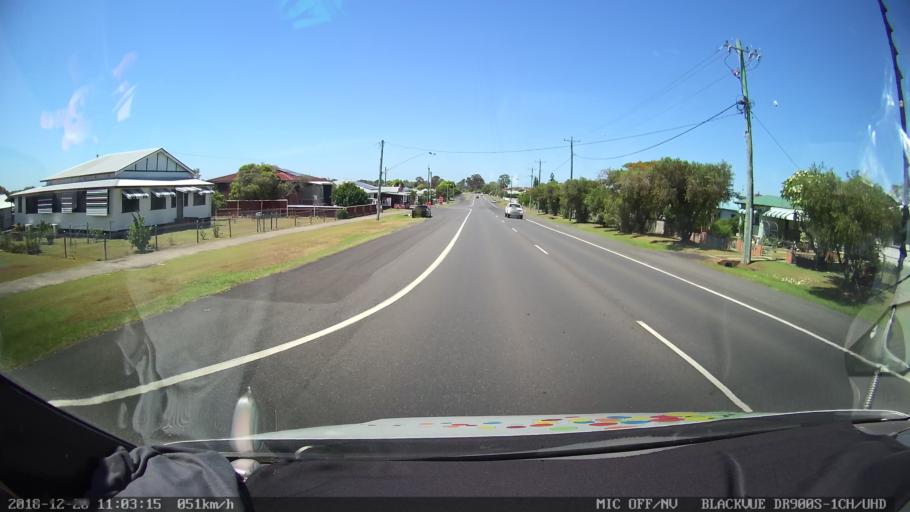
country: AU
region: New South Wales
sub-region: Richmond Valley
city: Casino
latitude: -28.8754
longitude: 153.0434
